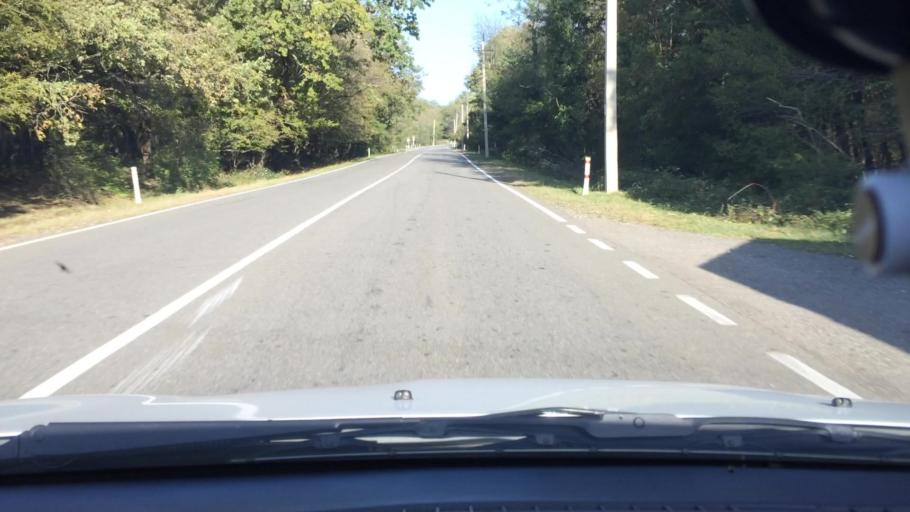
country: GE
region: Imereti
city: Kutaisi
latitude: 42.2459
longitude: 42.7584
